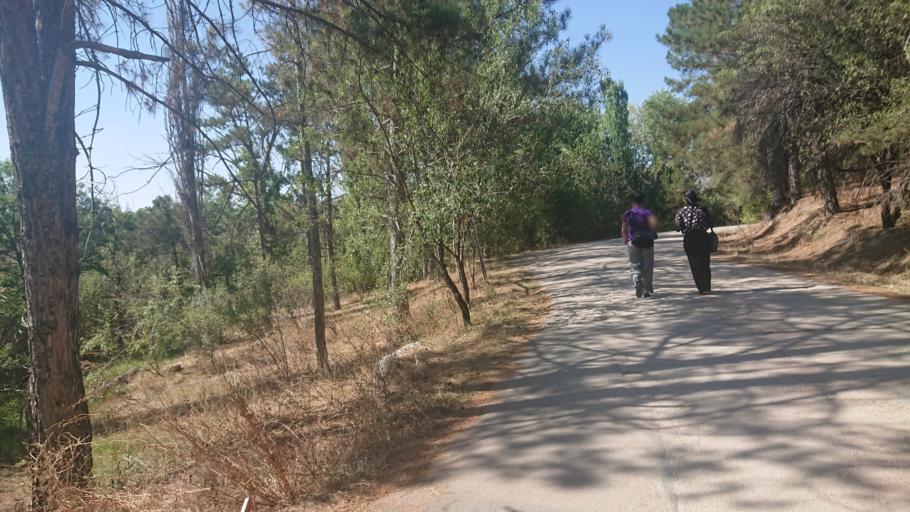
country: TR
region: Ankara
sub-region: Goelbasi
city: Golbasi
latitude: 39.8150
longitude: 32.8213
